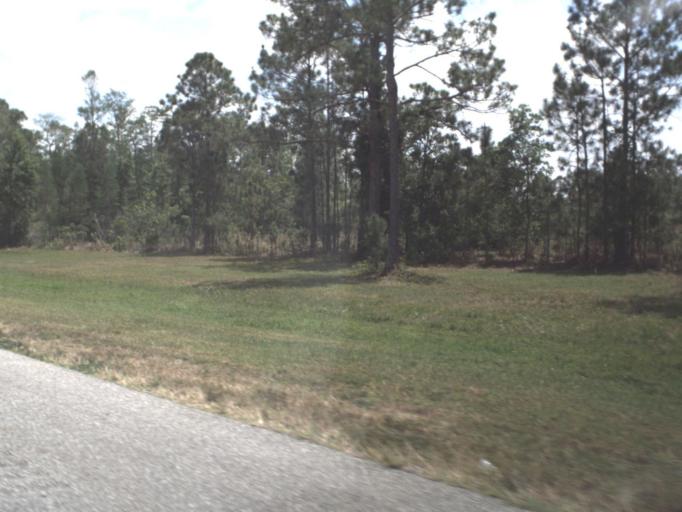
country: US
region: Florida
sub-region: Orange County
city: Wedgefield
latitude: 28.4521
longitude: -81.0457
